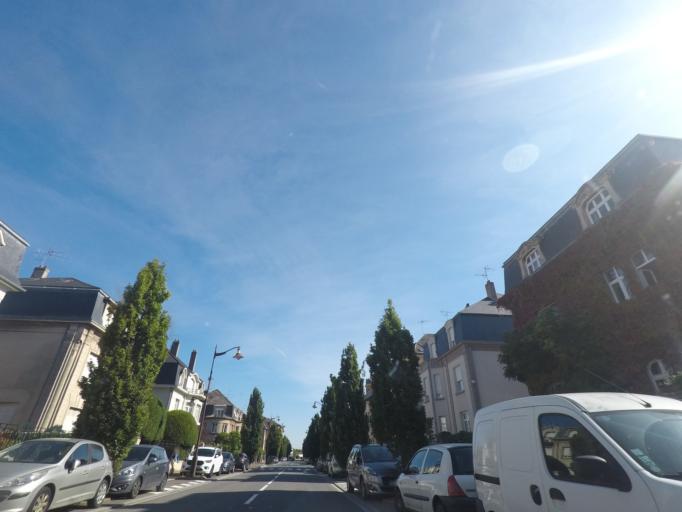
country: FR
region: Lorraine
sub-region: Departement de la Moselle
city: Thionville
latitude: 49.3620
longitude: 6.1667
